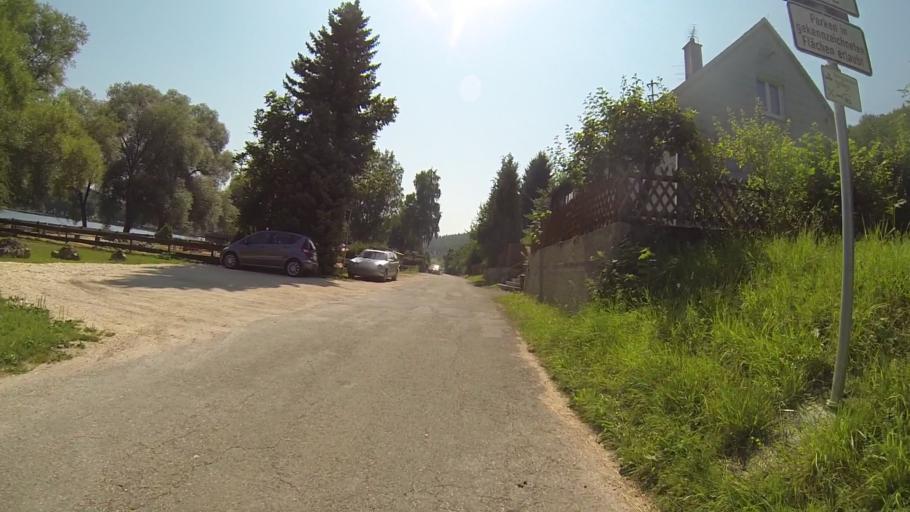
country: DE
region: Baden-Wuerttemberg
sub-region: Regierungsbezirk Stuttgart
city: Konigsbronn
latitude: 48.7325
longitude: 10.1301
